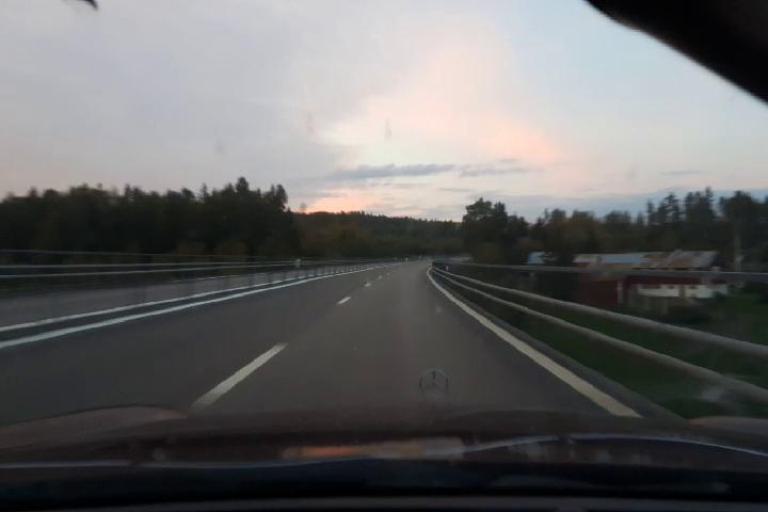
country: SE
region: Vaesternorrland
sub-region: Haernoesands Kommun
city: Haernoesand
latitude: 62.8383
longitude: 17.9711
